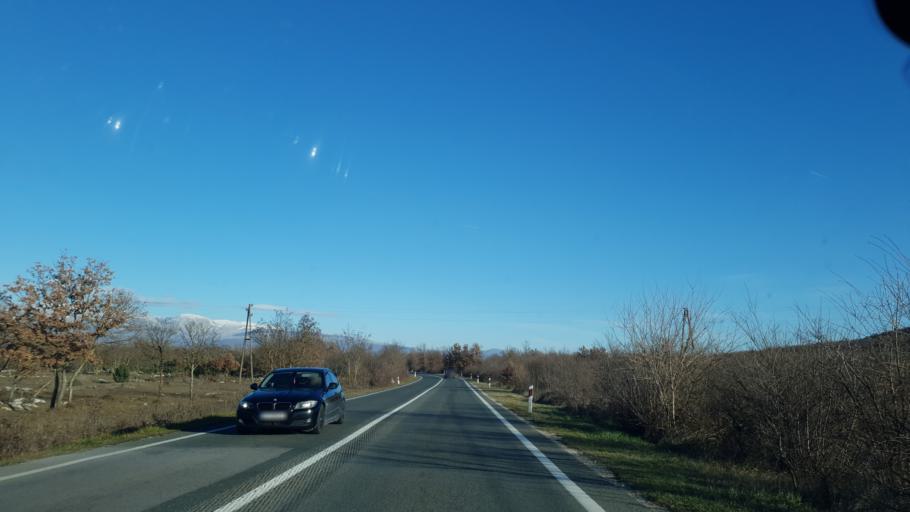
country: HR
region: Splitsko-Dalmatinska
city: Brnaze
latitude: 43.6424
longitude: 16.6144
